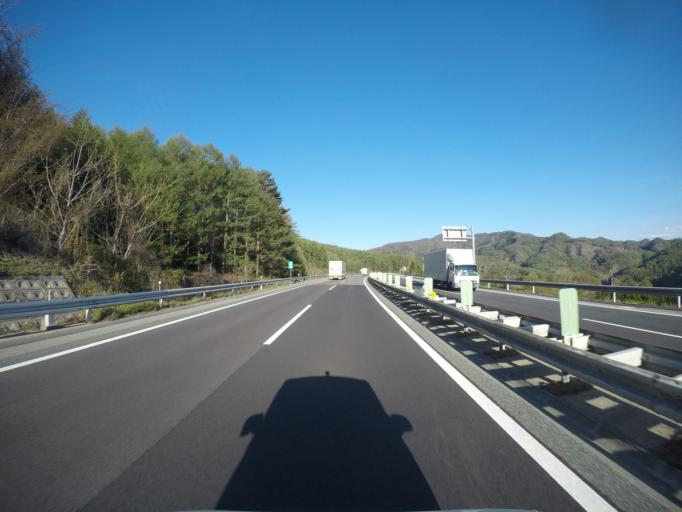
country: JP
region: Nagano
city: Saku
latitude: 36.2718
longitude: 138.5604
